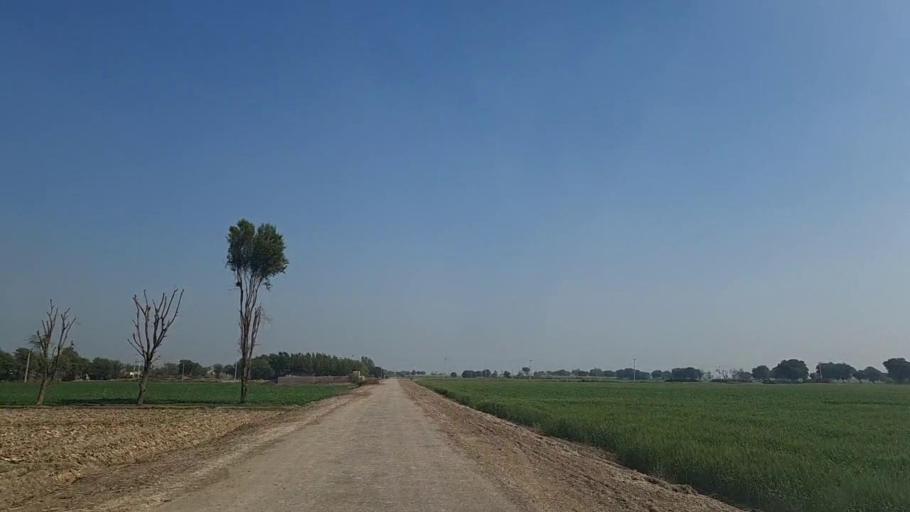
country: PK
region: Sindh
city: Shahpur Chakar
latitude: 26.2027
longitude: 68.5712
